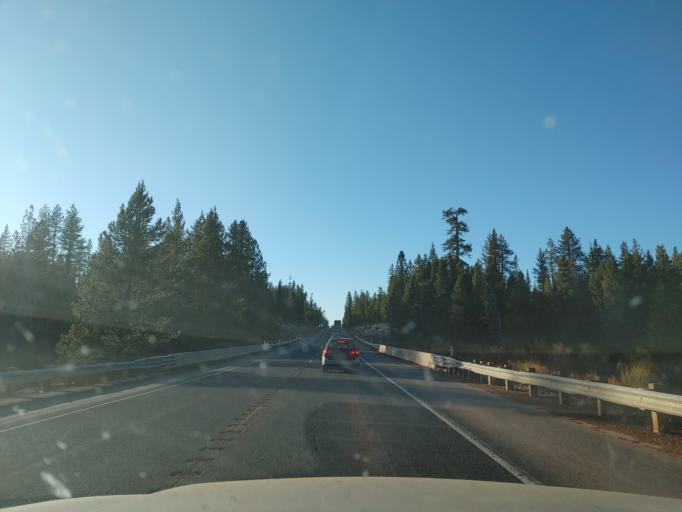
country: US
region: Oregon
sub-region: Deschutes County
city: La Pine
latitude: 43.3798
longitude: -121.8005
